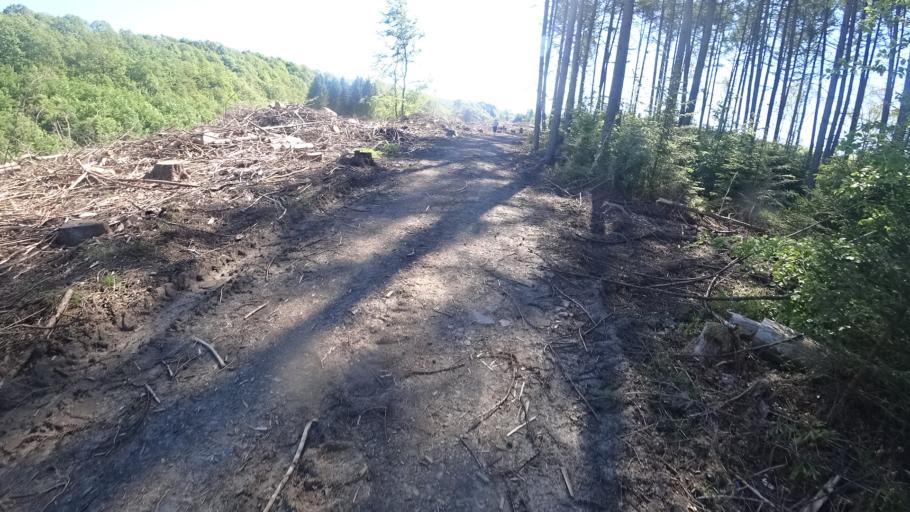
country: DE
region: Rheinland-Pfalz
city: Dickendorf
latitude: 50.7366
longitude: 7.8582
